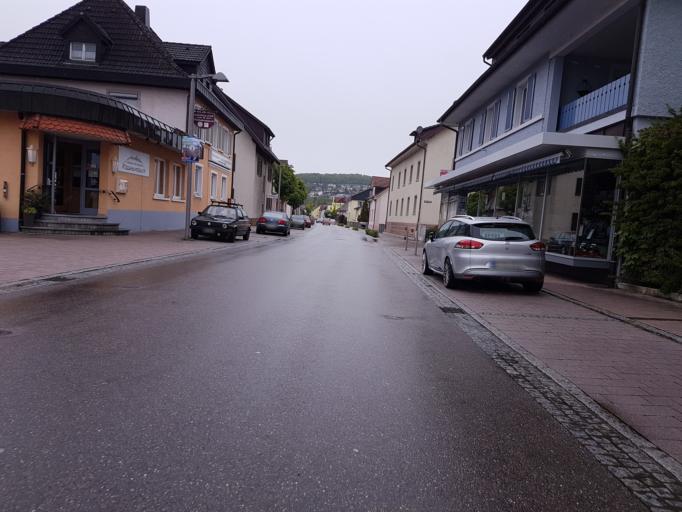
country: DE
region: Baden-Wuerttemberg
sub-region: Freiburg Region
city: Lauchringen
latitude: 47.6296
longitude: 8.3020
